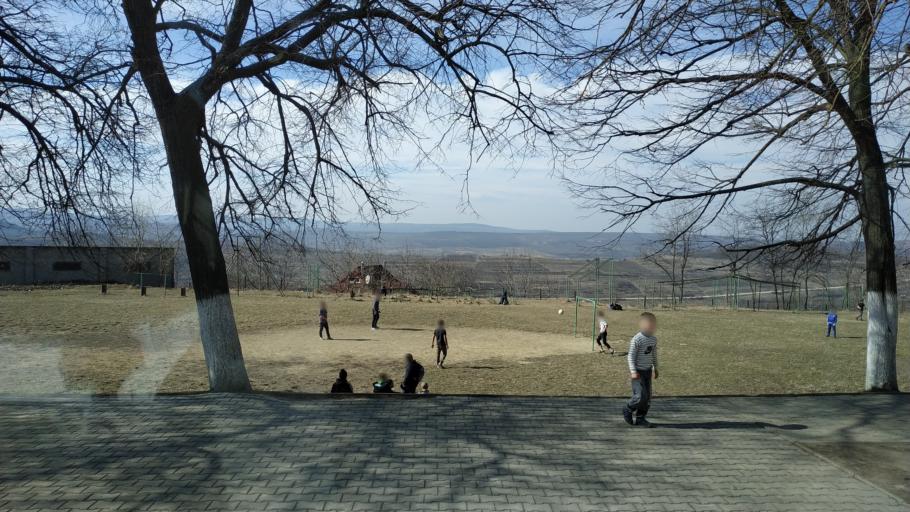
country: MD
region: Nisporeni
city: Nisporeni
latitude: 47.2260
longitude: 28.0402
